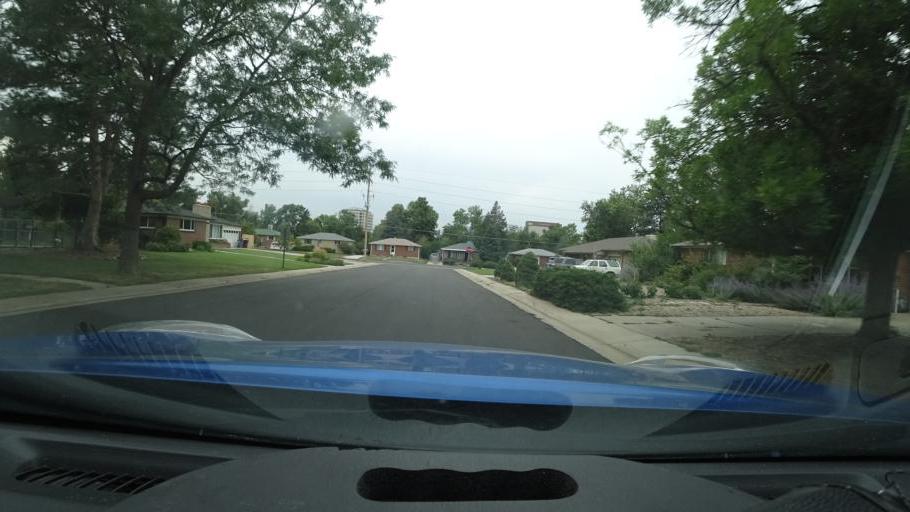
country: US
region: Colorado
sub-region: Arapahoe County
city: Glendale
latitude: 39.6813
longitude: -104.9309
